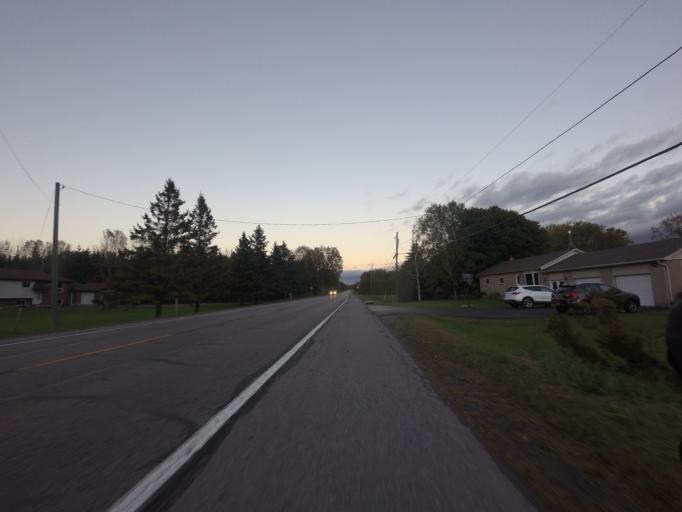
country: CA
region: Ontario
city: Quinte West
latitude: 44.0398
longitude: -77.6832
